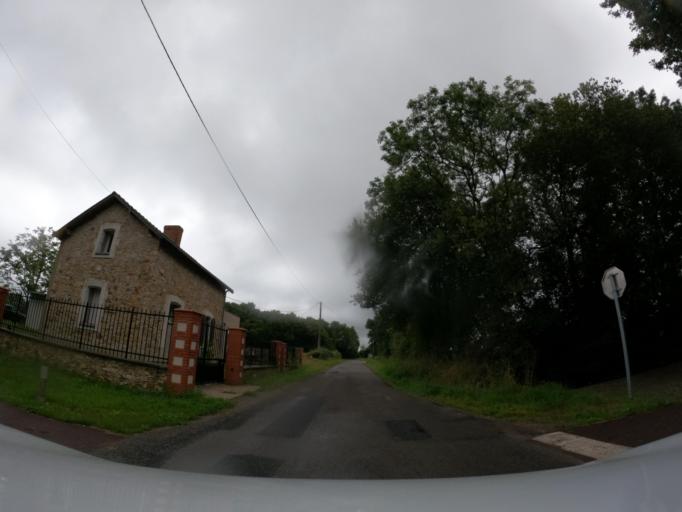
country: FR
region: Pays de la Loire
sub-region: Departement de la Loire-Atlantique
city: Saint-Mars-du-Desert
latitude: 47.3719
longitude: -1.3853
